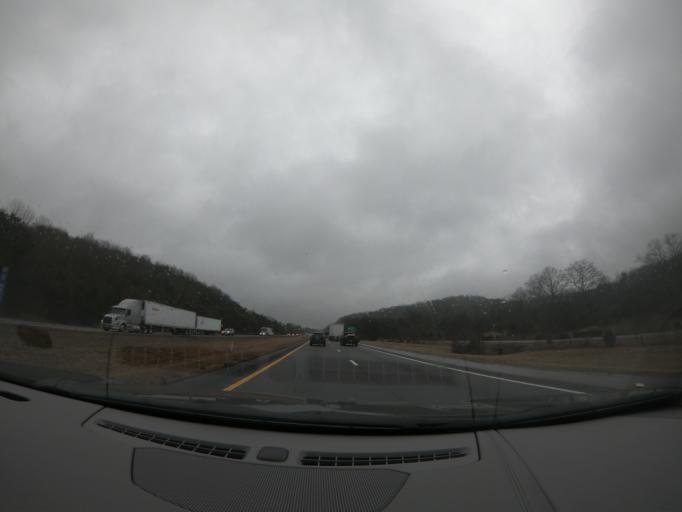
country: US
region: Tennessee
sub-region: Rutherford County
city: Plainview
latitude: 35.6421
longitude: -86.2515
